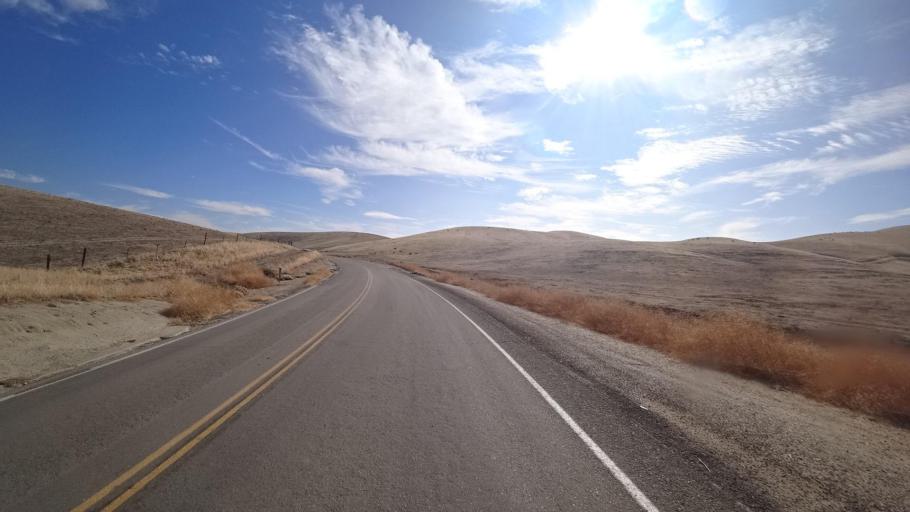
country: US
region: California
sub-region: Kern County
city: Oildale
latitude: 35.6041
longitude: -118.9506
